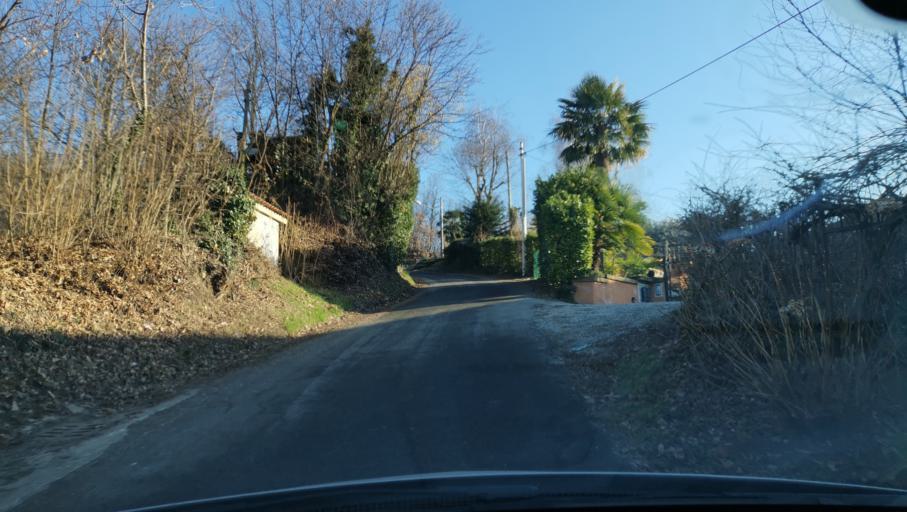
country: IT
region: Piedmont
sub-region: Provincia di Torino
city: San Raffaele Cimena
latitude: 45.1400
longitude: 7.8675
